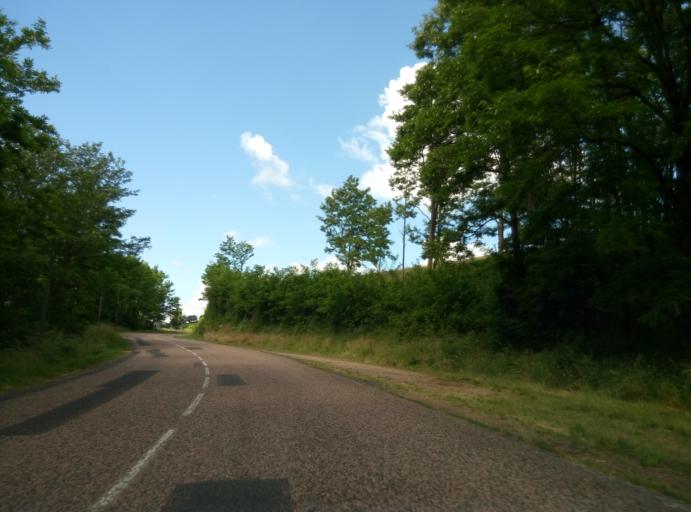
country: FR
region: Rhone-Alpes
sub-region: Departement du Rhone
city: Thizy-les-Bourgs
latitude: 46.0193
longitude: 4.3212
